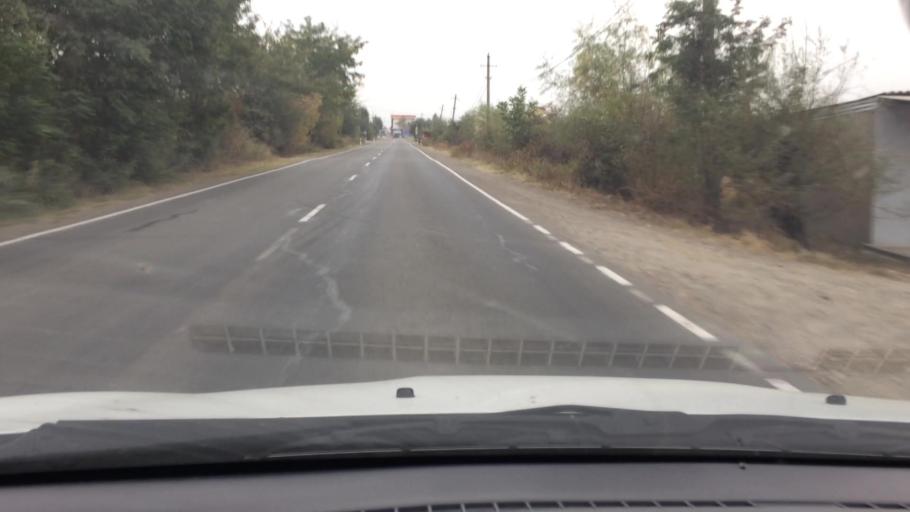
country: GE
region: Kvemo Kartli
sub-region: Marneuli
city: Marneuli
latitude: 41.4634
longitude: 44.8088
